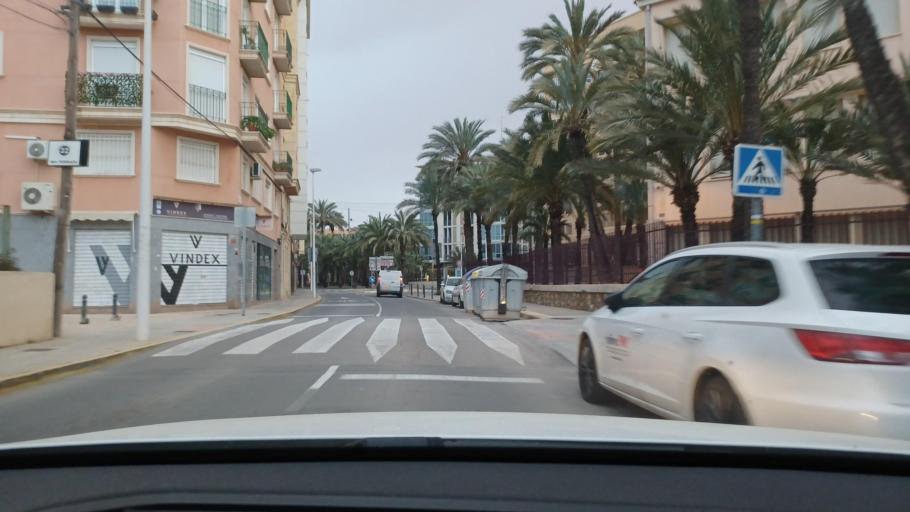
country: ES
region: Valencia
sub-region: Provincia de Alicante
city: Elche
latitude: 38.2616
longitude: -0.6938
